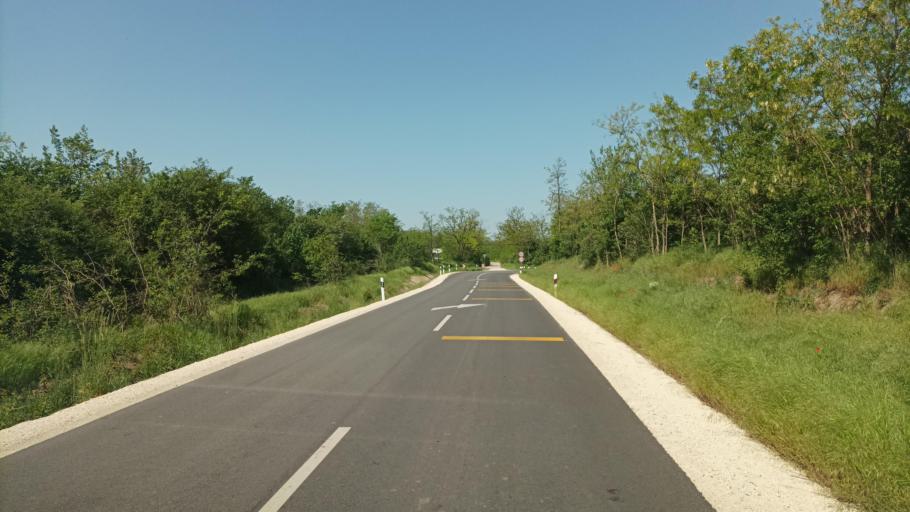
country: HU
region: Pest
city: Gomba
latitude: 47.3845
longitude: 19.5033
